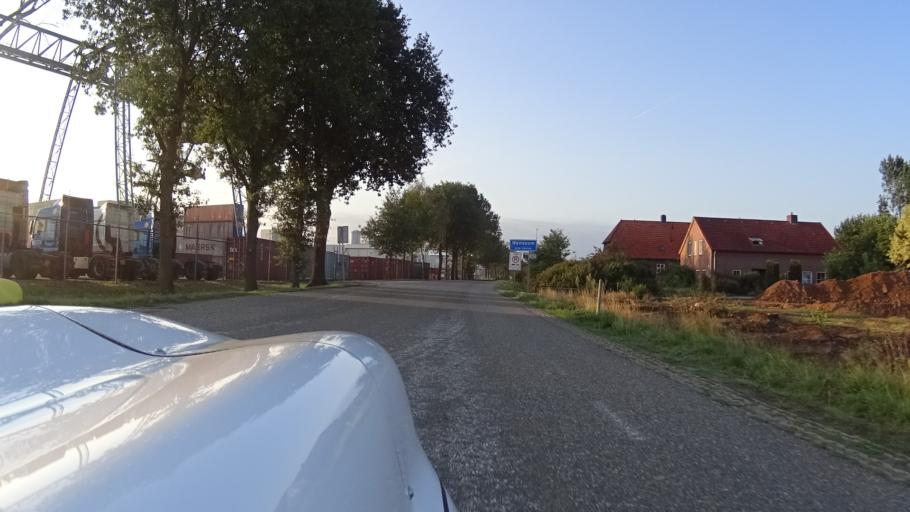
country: NL
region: Limburg
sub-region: Gemeente Bergen
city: Wellerlooi
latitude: 51.5439
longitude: 6.0744
